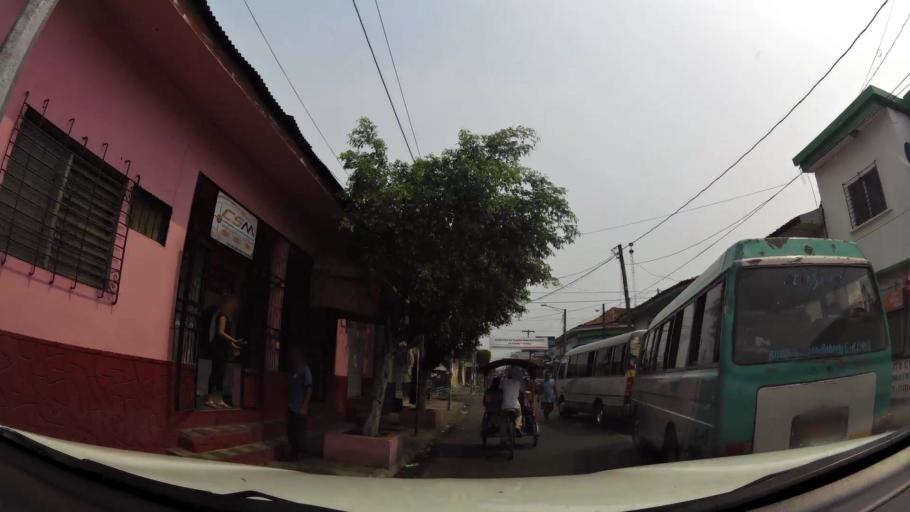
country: NI
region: Chinandega
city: Chinandega
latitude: 12.6319
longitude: -87.1312
